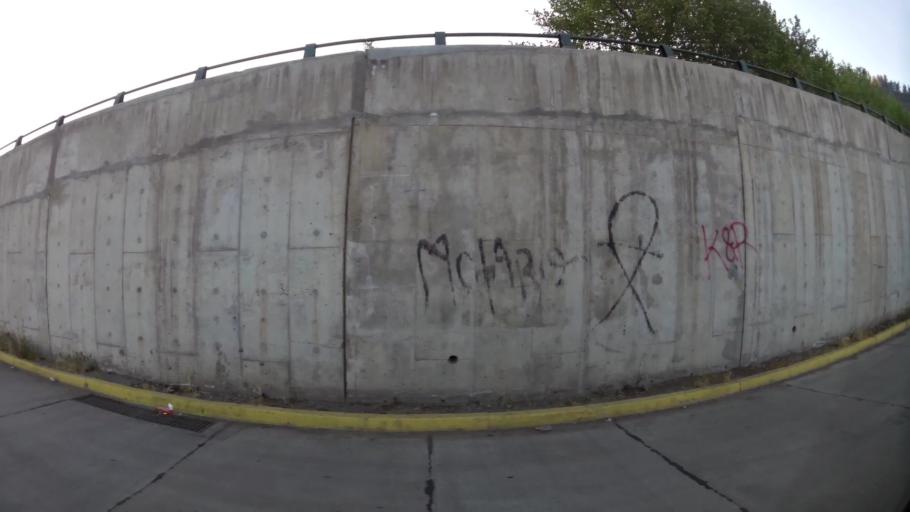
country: CL
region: Santiago Metropolitan
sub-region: Provincia de Santiago
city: Santiago
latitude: -33.3944
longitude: -70.6127
